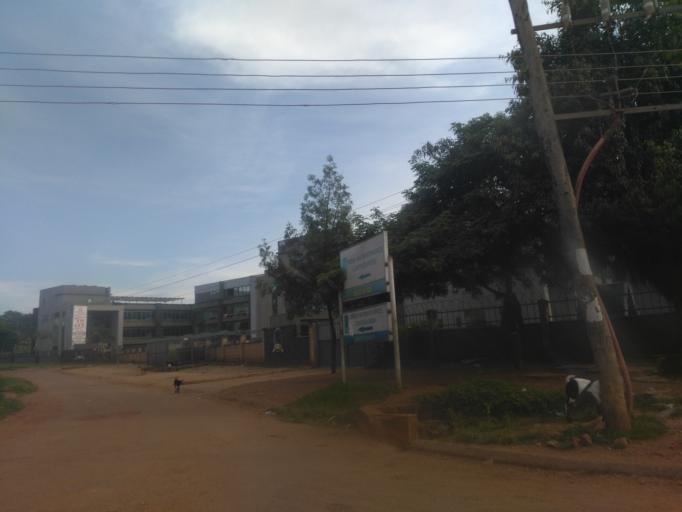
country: UG
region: Central Region
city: Kampala Central Division
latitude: 0.3452
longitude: 32.5937
